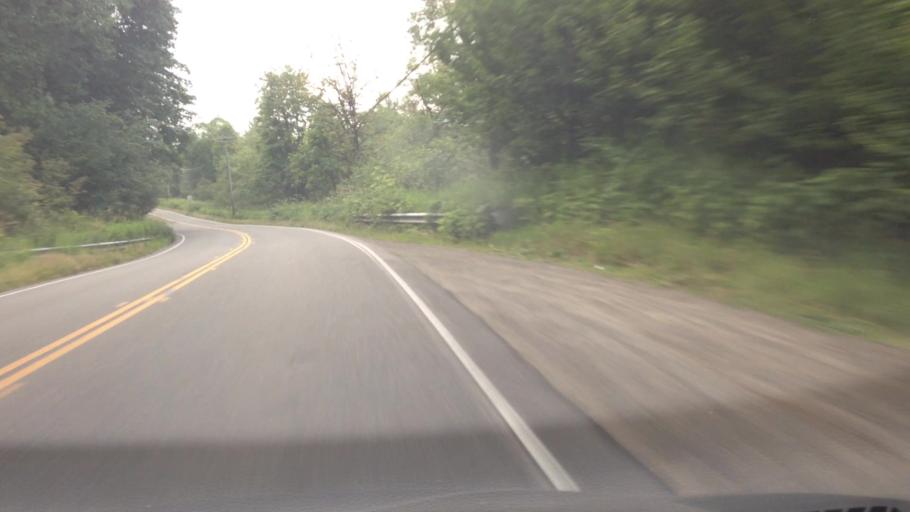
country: US
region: Washington
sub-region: King County
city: Duvall
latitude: 47.7477
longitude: -121.9612
